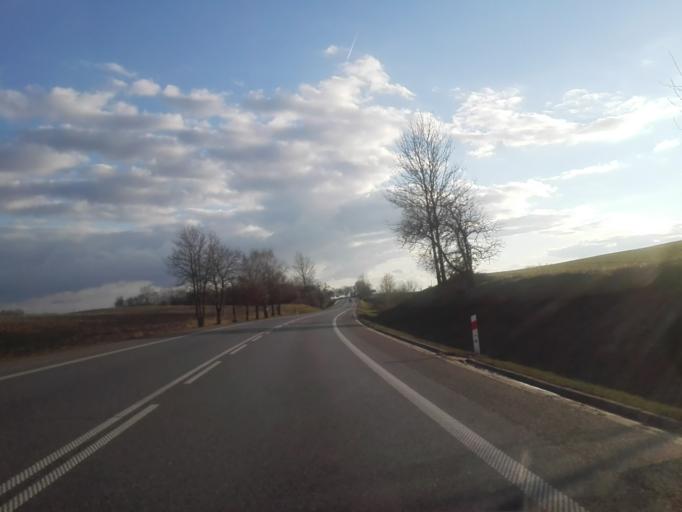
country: PL
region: Podlasie
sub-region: Suwalki
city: Suwalki
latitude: 54.1910
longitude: 23.0102
